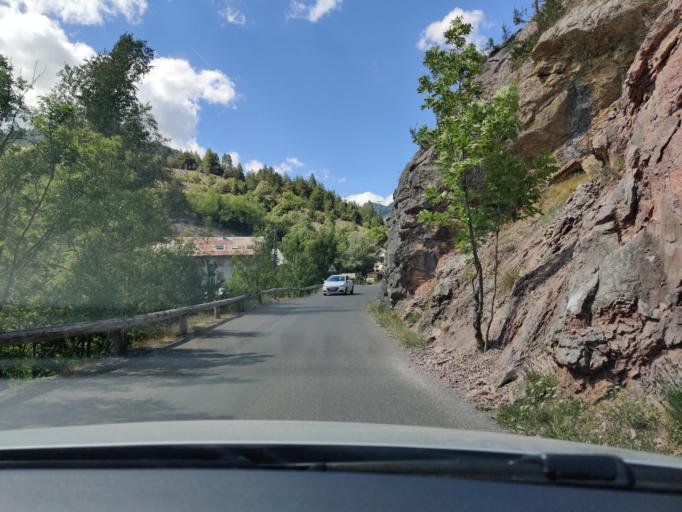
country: FR
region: Provence-Alpes-Cote d'Azur
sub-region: Departement des Hautes-Alpes
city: Saint-Martin-de-Queyrieres
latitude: 44.7378
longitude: 6.5652
